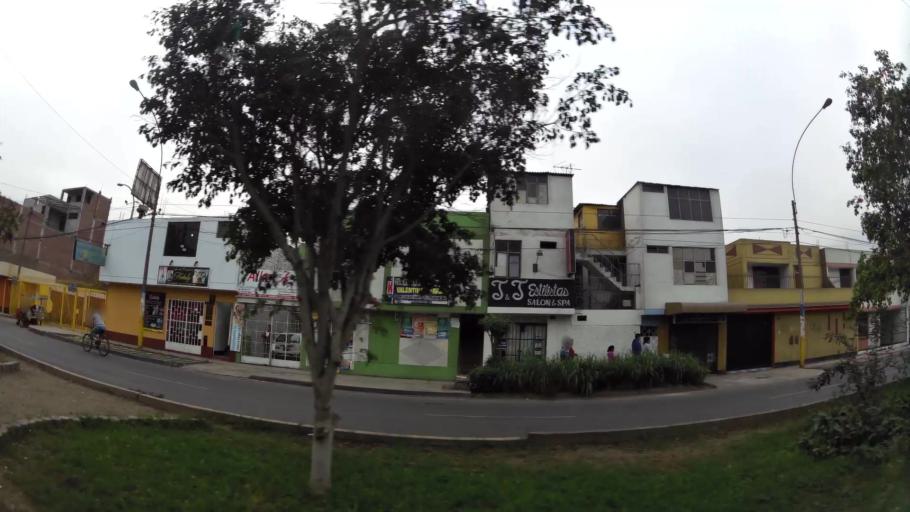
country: PE
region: Lima
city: Lima
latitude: -12.0124
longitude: -77.0105
